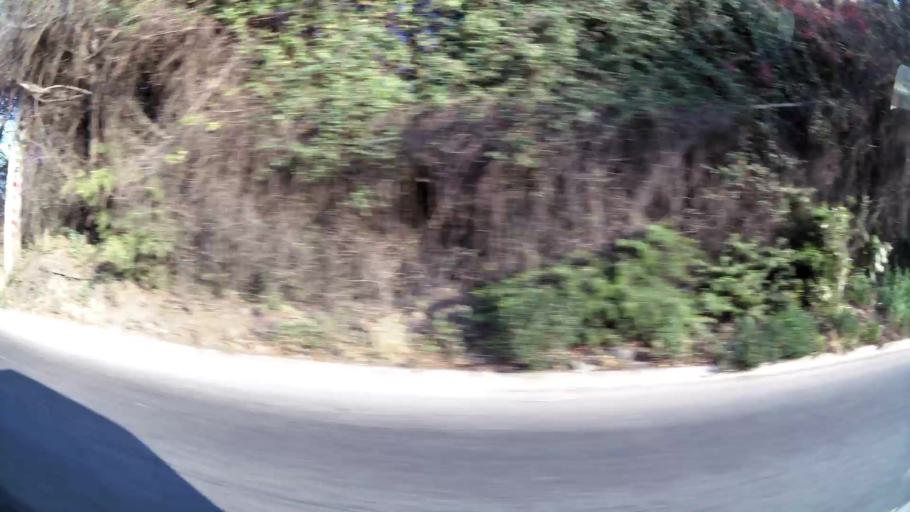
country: CL
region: Santiago Metropolitan
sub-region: Provincia de Santiago
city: Villa Presidente Frei, Nunoa, Santiago, Chile
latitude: -33.3549
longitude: -70.5272
